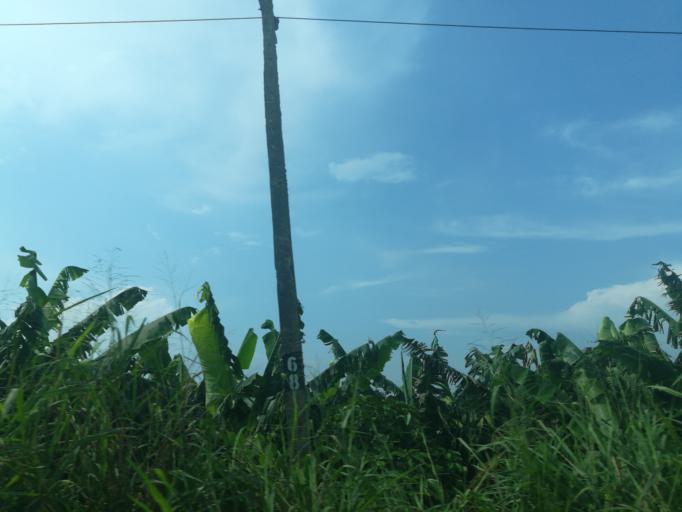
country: NG
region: Lagos
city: Ikorodu
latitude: 6.6312
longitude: 3.5266
